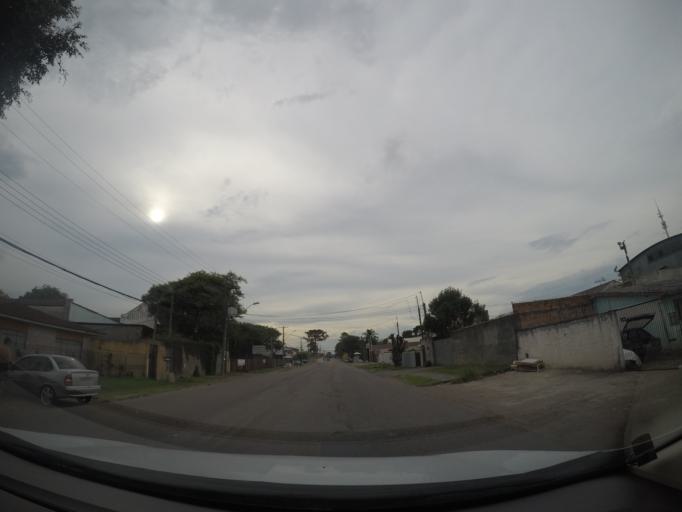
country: BR
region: Parana
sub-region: Sao Jose Dos Pinhais
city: Sao Jose dos Pinhais
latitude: -25.5023
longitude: -49.2260
